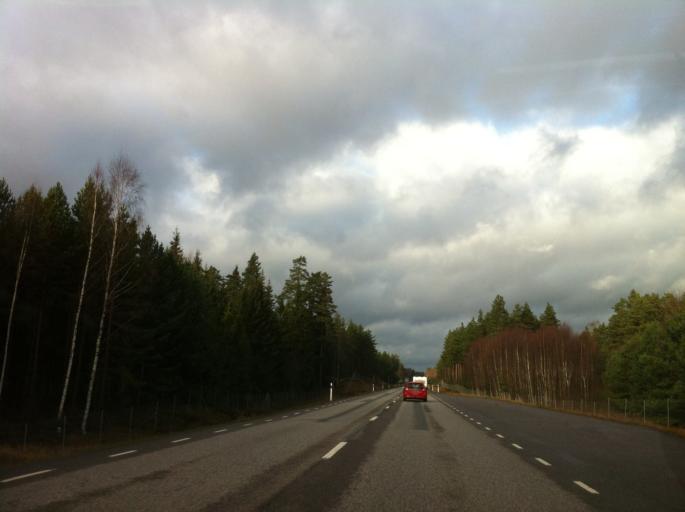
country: SE
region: Kalmar
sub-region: Vimmerby Kommun
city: Vimmerby
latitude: 57.6216
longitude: 15.8421
